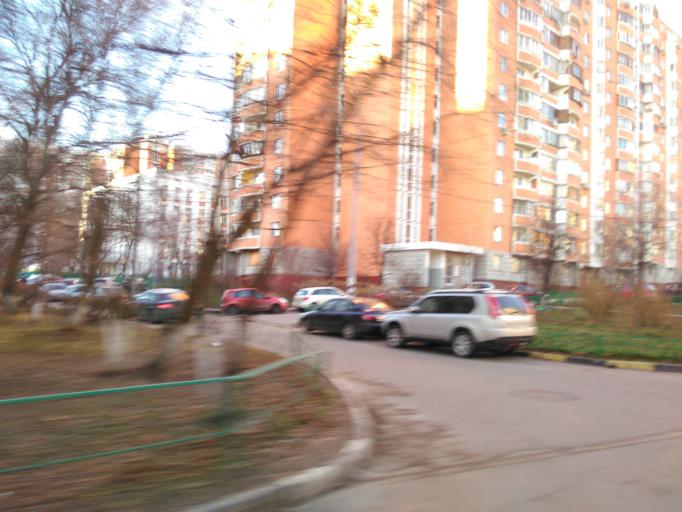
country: RU
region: Moscow
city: Nagornyy
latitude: 55.6495
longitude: 37.6100
